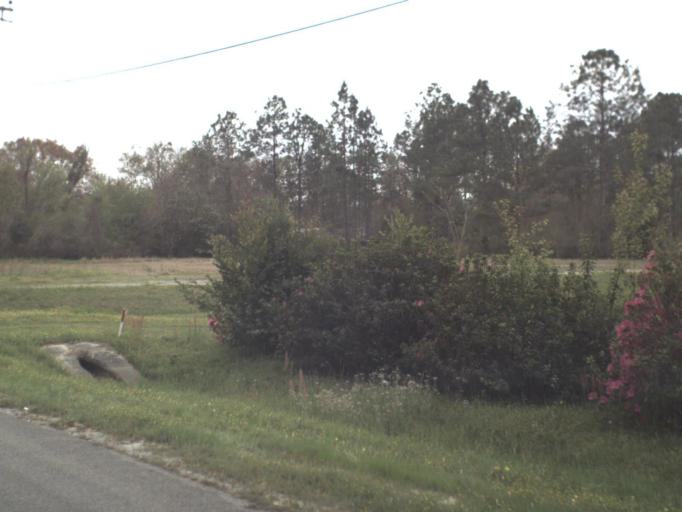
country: US
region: Florida
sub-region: Gulf County
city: Wewahitchka
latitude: 30.0902
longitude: -85.1951
